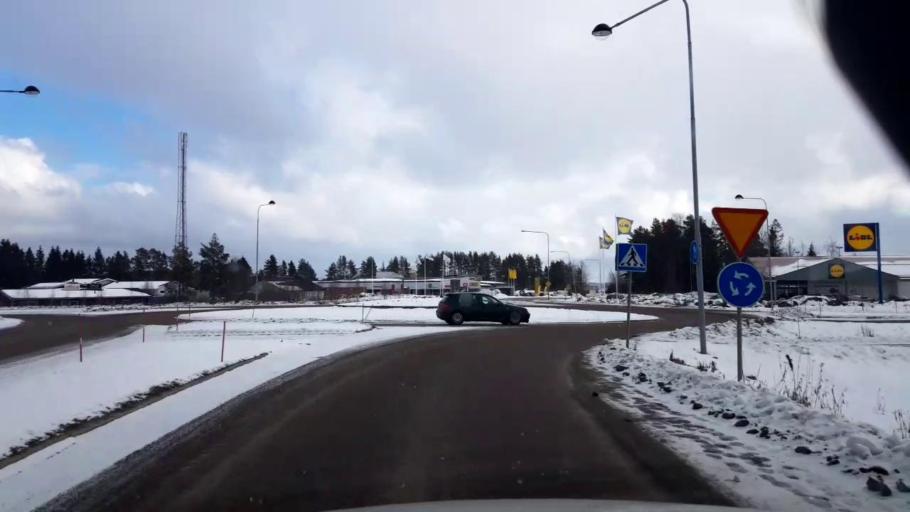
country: SE
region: Gaevleborg
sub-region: Hudiksvalls Kommun
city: Hudiksvall
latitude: 61.7387
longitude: 17.0860
